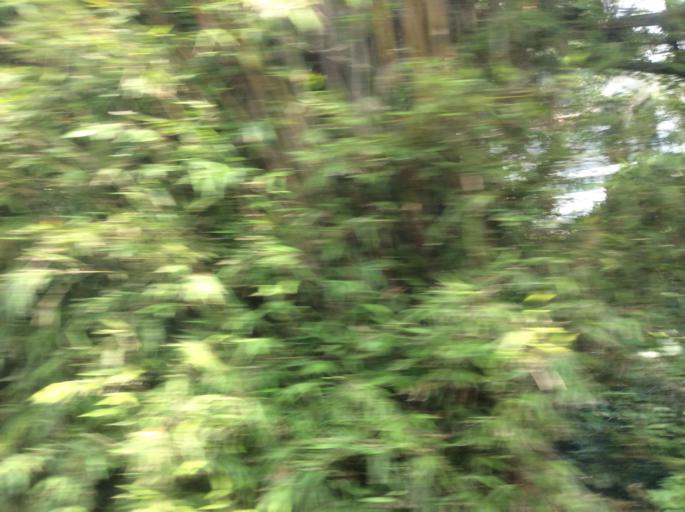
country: TW
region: Taipei
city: Taipei
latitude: 25.1523
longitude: 121.5461
